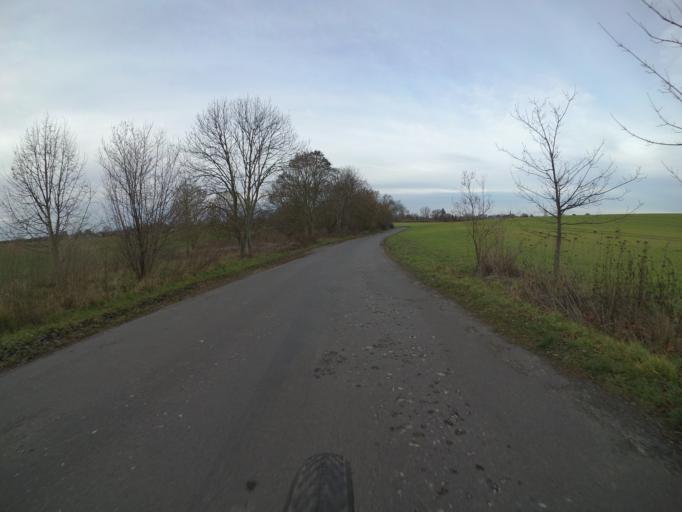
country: DE
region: Brandenburg
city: Schoneiche
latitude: 52.4850
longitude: 13.6791
